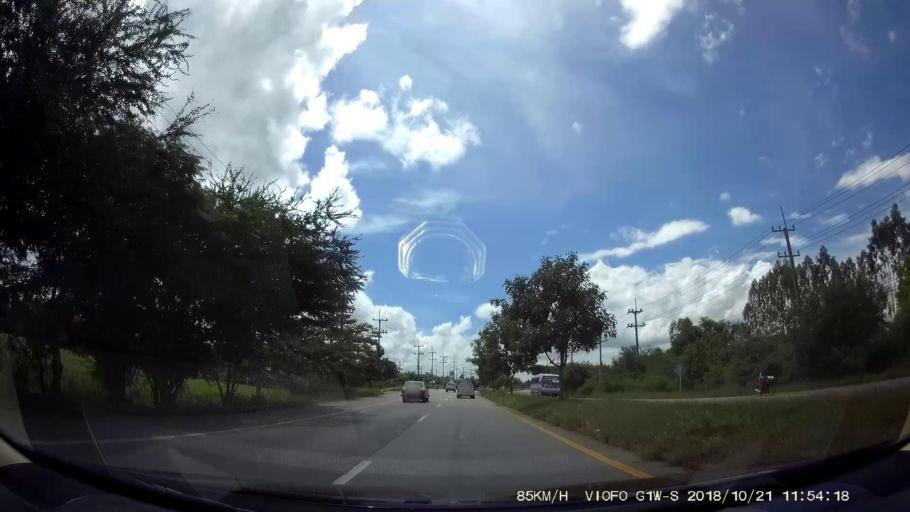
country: TH
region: Chaiyaphum
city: Chatturat
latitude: 15.5859
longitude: 101.9019
